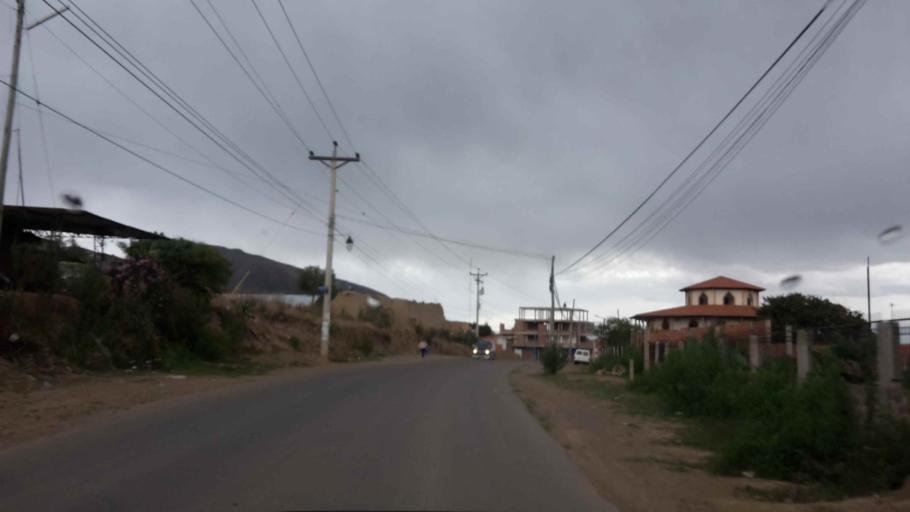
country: BO
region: Cochabamba
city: Tarata
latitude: -17.6085
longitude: -66.0275
